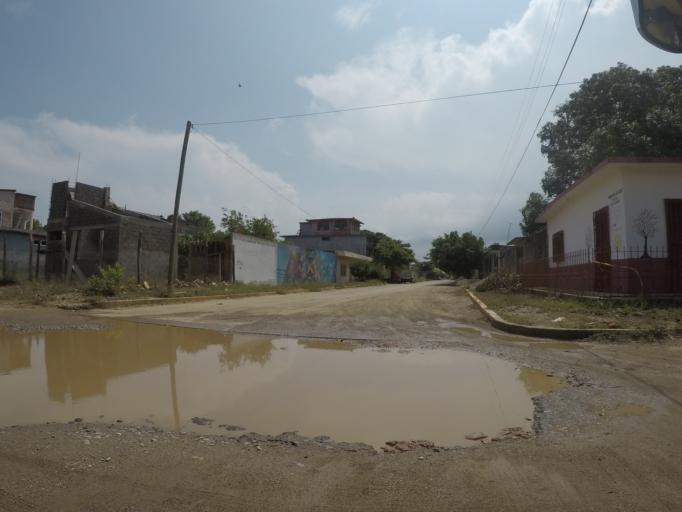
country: MX
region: Oaxaca
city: Union Hidalgo
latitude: 16.4745
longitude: -94.8325
